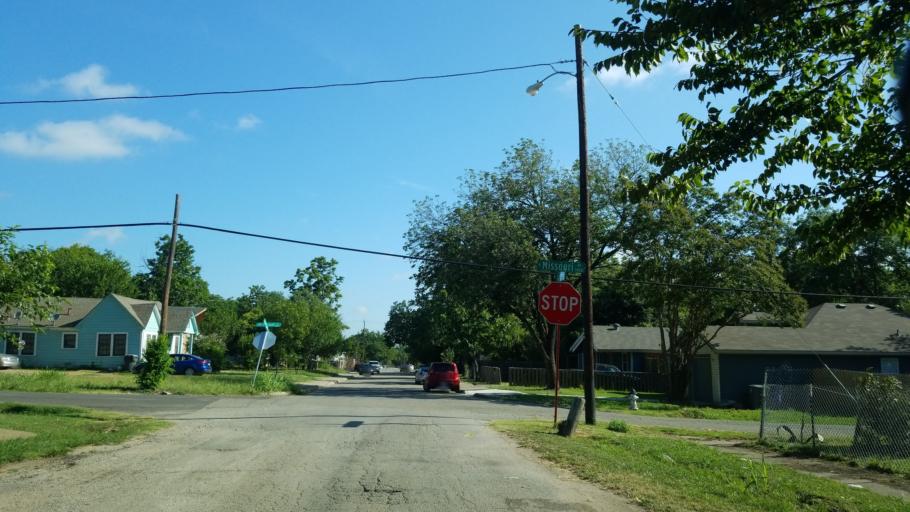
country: US
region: Texas
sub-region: Dallas County
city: Dallas
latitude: 32.7176
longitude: -96.8098
